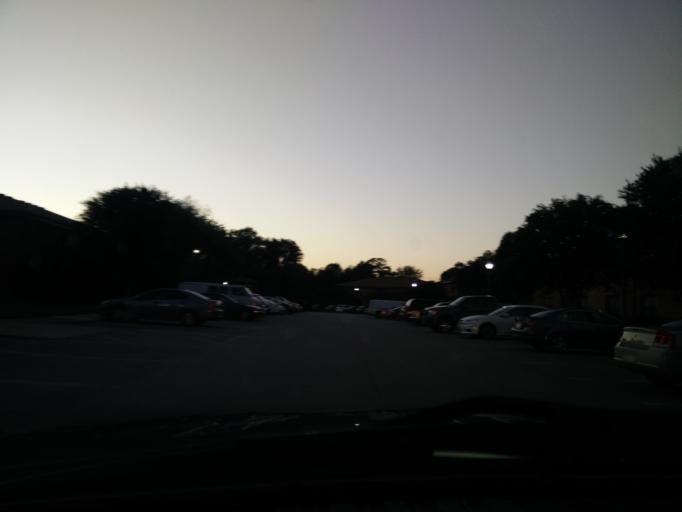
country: US
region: Virginia
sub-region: City of Chesapeake
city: Chesapeake
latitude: 36.7485
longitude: -76.2348
